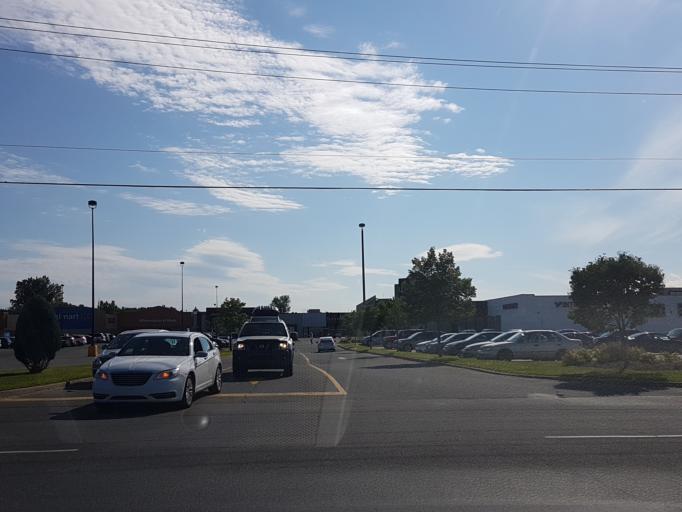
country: CA
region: Quebec
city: Sainte-Catherine
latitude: 46.3266
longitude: -72.5648
